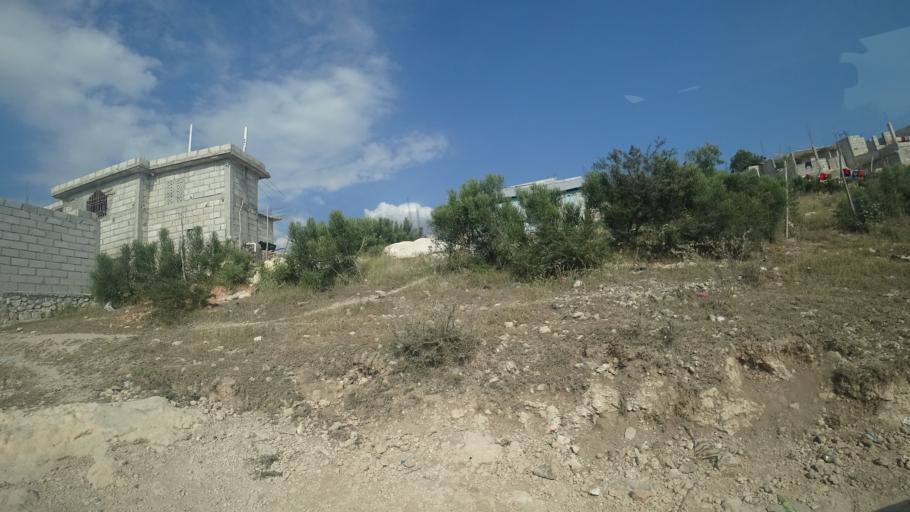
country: HT
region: Ouest
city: Croix des Bouquets
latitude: 18.6620
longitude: -72.2823
